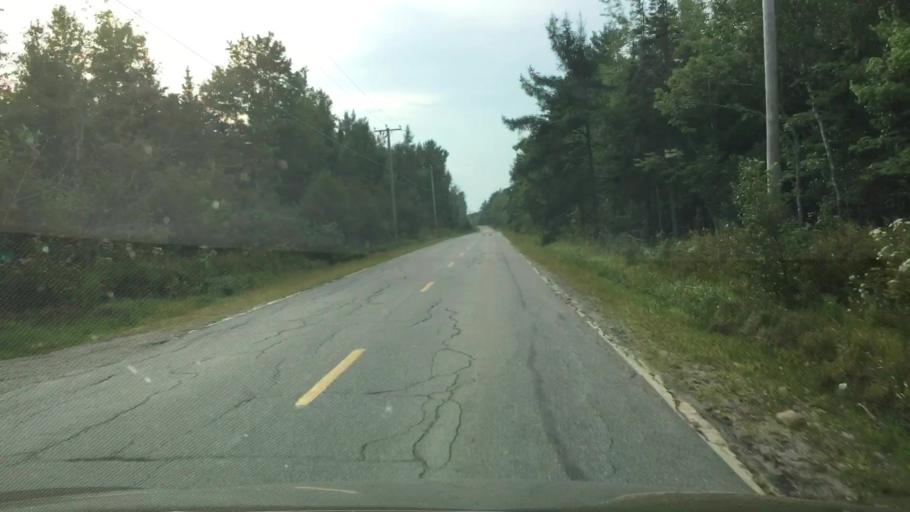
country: US
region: Maine
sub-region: Hancock County
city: Penobscot
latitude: 44.4709
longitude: -68.7481
